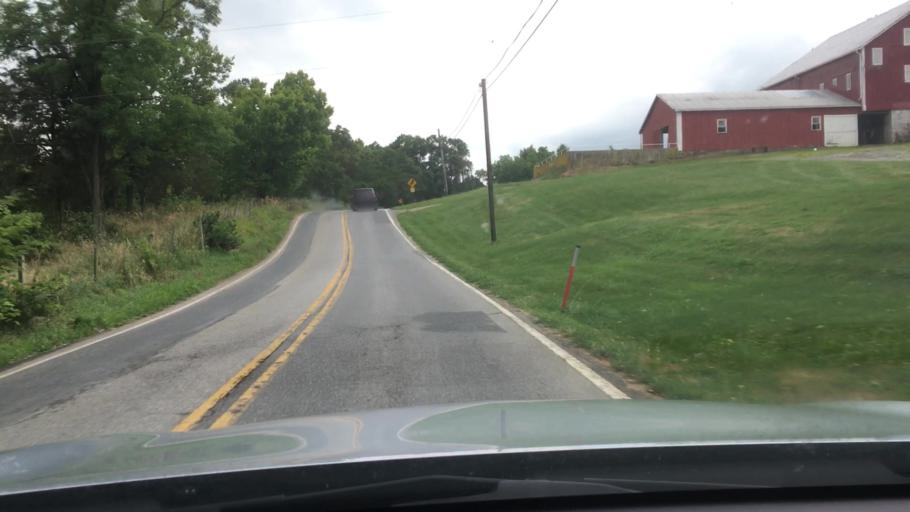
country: US
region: Pennsylvania
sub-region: Franklin County
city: Greencastle
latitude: 39.8627
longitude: -77.7960
